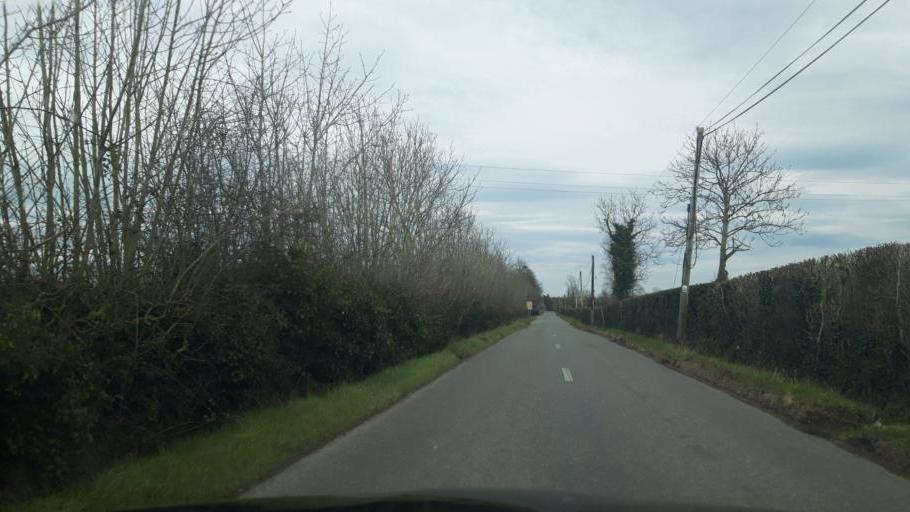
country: IE
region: Leinster
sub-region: Kildare
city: Rathangan
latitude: 53.2405
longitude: -6.9575
